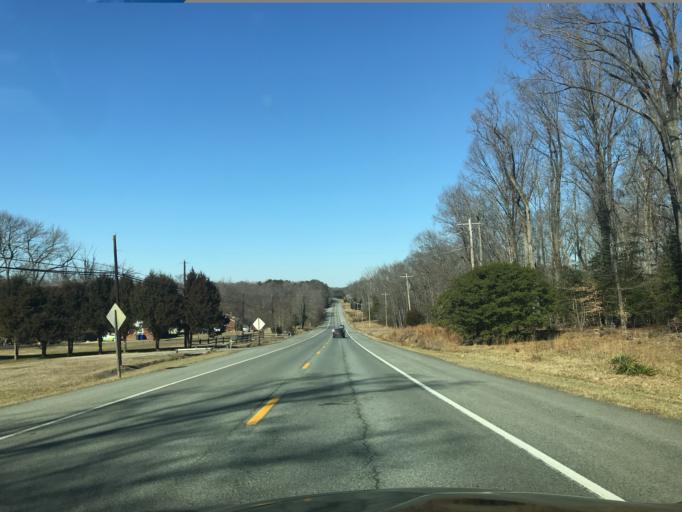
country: US
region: Maryland
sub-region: Charles County
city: Bryans Road
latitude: 38.6507
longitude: -77.0759
